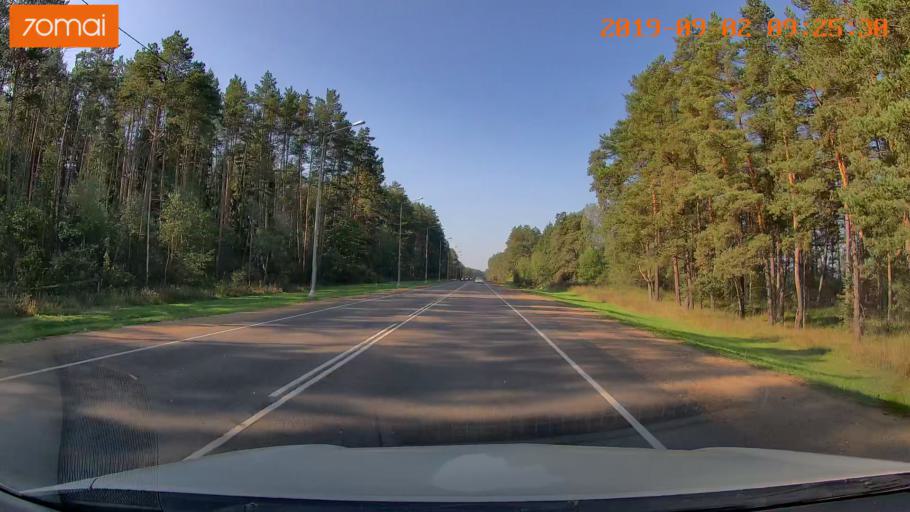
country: RU
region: Kaluga
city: Yukhnov
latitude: 54.7578
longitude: 35.2766
